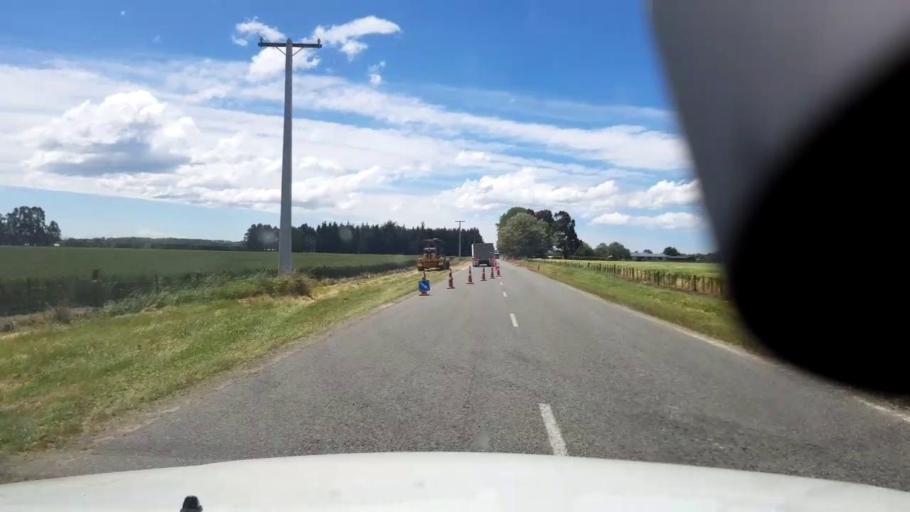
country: NZ
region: Canterbury
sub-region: Timaru District
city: Pleasant Point
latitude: -44.2796
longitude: 171.2469
